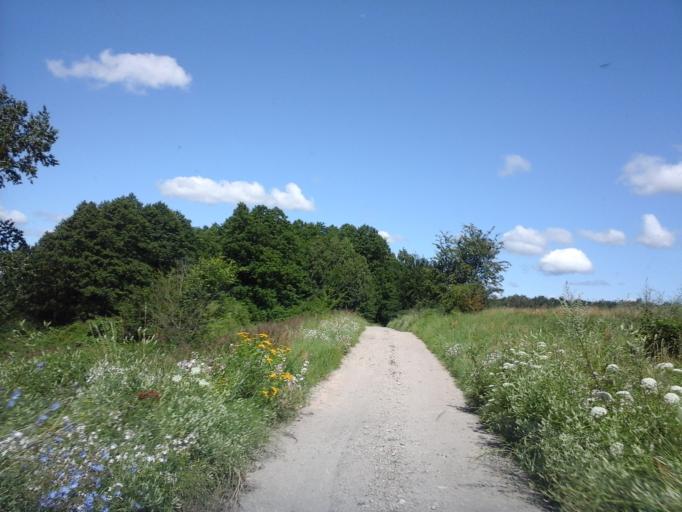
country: PL
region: West Pomeranian Voivodeship
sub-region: Powiat choszczenski
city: Recz
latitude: 53.2382
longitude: 15.5600
